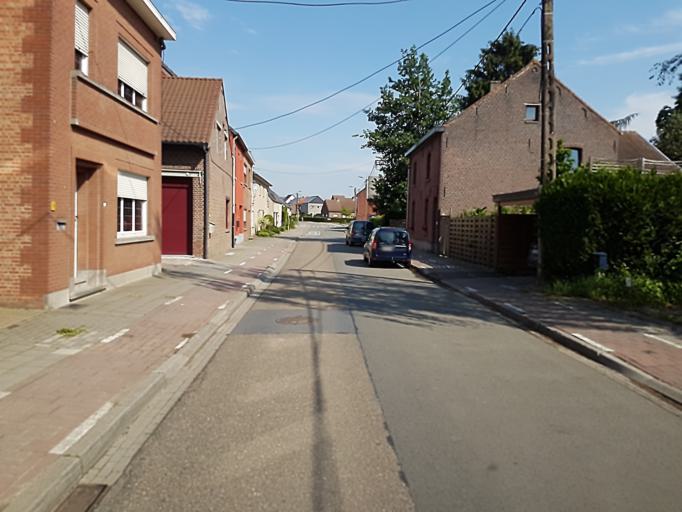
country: BE
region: Flanders
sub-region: Provincie Vlaams-Brabant
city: Herent
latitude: 50.9163
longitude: 4.6984
